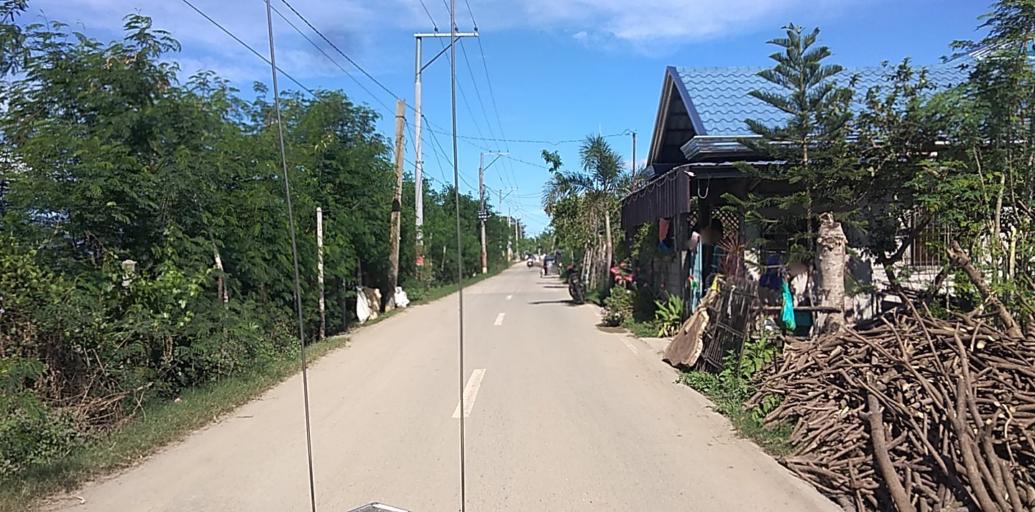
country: PH
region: Central Luzon
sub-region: Province of Pampanga
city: Candaba
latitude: 15.1192
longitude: 120.8137
